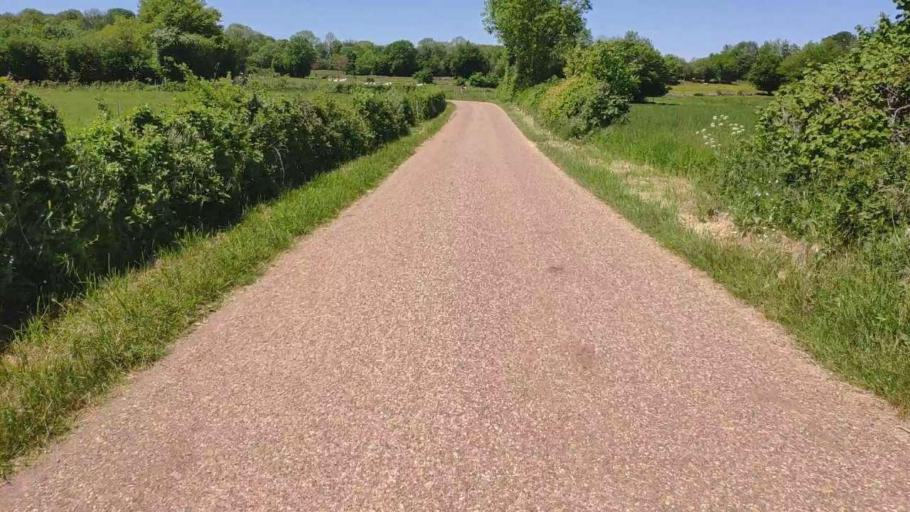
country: FR
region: Franche-Comte
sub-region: Departement du Jura
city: Poligny
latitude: 46.7386
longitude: 5.6825
